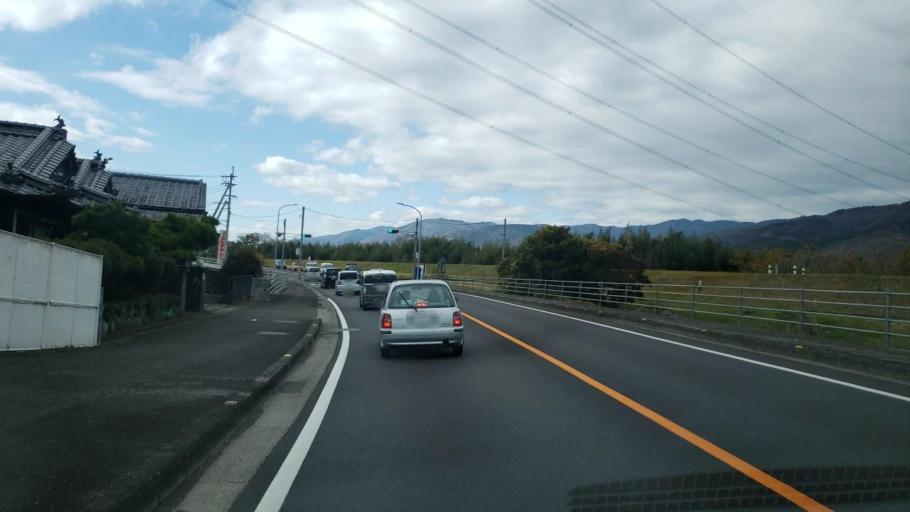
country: JP
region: Tokushima
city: Wakimachi
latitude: 34.0567
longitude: 134.1262
